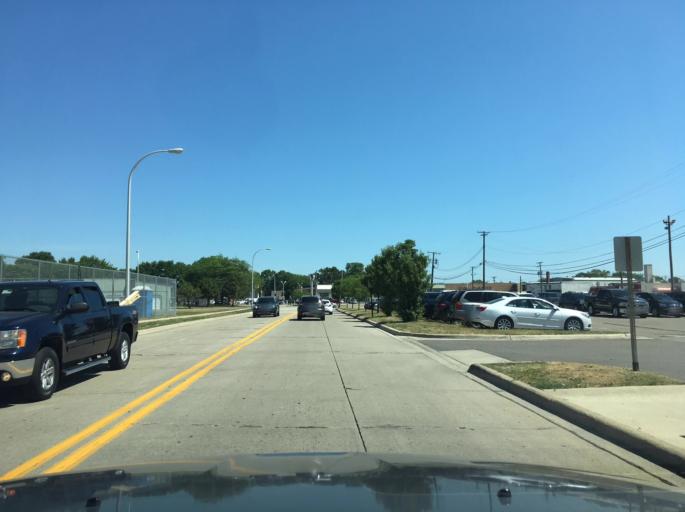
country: US
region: Michigan
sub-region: Wayne County
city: Grosse Pointe Woods
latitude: 42.4648
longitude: -82.9000
